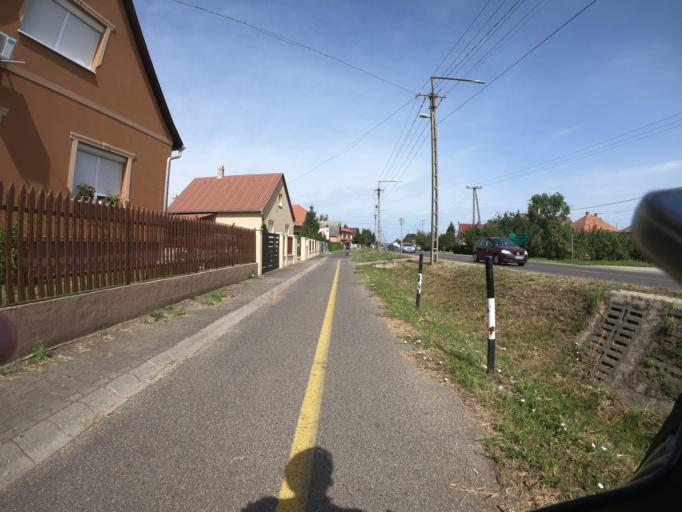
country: HU
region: Jasz-Nagykun-Szolnok
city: Tiszafured
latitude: 47.6072
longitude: 20.7576
